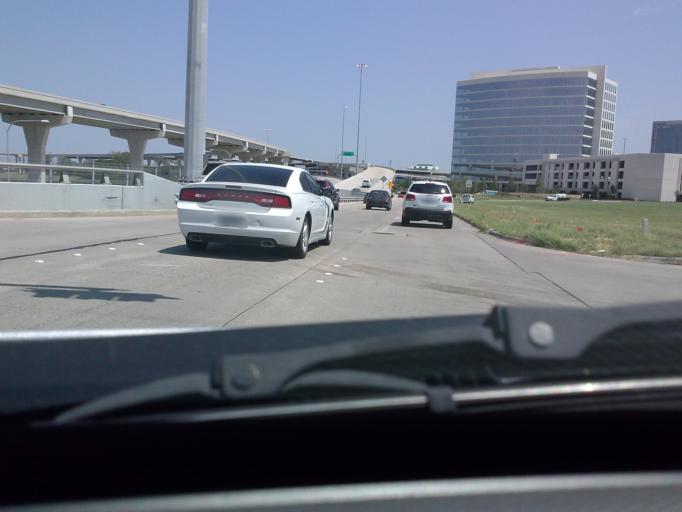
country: US
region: Texas
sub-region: Denton County
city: The Colony
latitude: 33.0842
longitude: -96.8235
